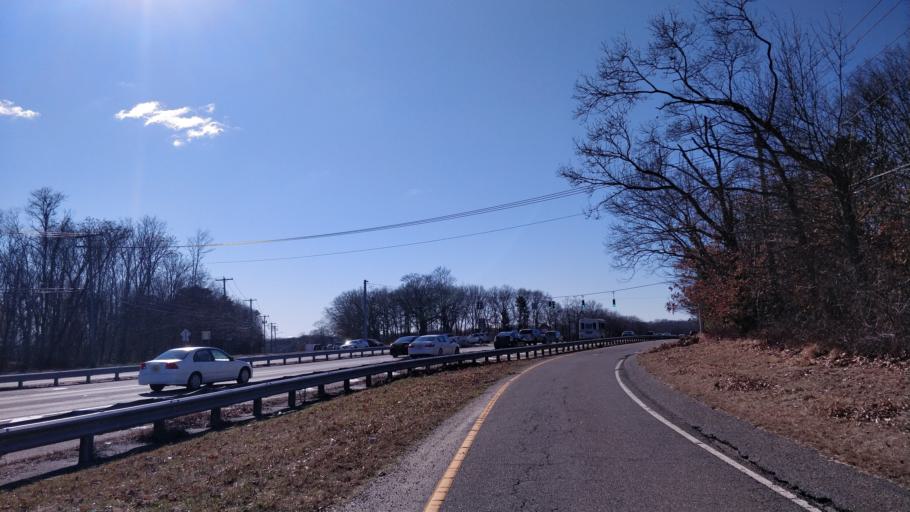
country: US
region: New York
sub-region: Suffolk County
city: Centereach
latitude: 40.8866
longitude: -73.1015
